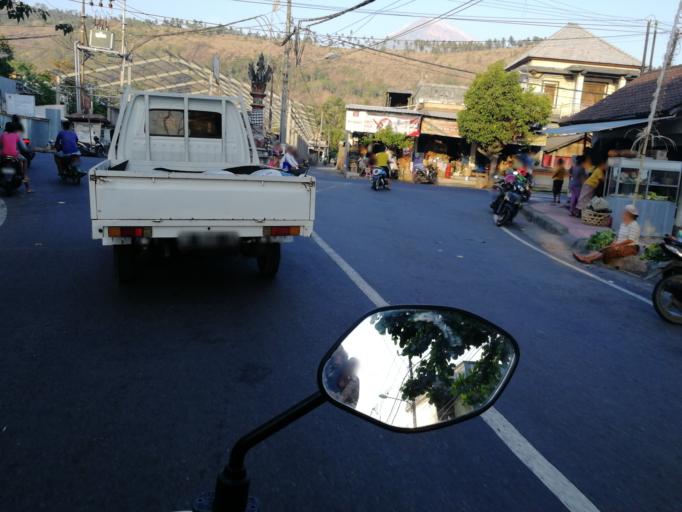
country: ID
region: Bali
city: Banjar Buayang
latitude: -8.3446
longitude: 115.6145
